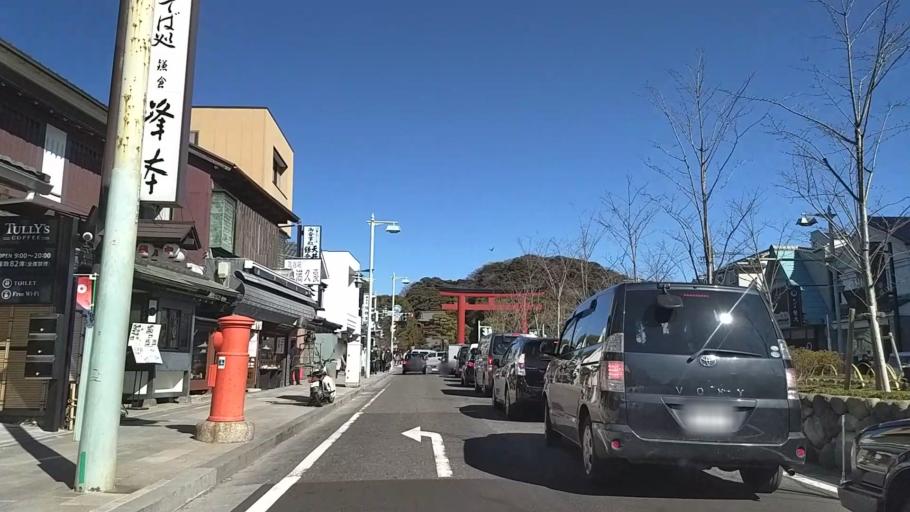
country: JP
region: Kanagawa
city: Kamakura
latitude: 35.3232
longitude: 139.5546
